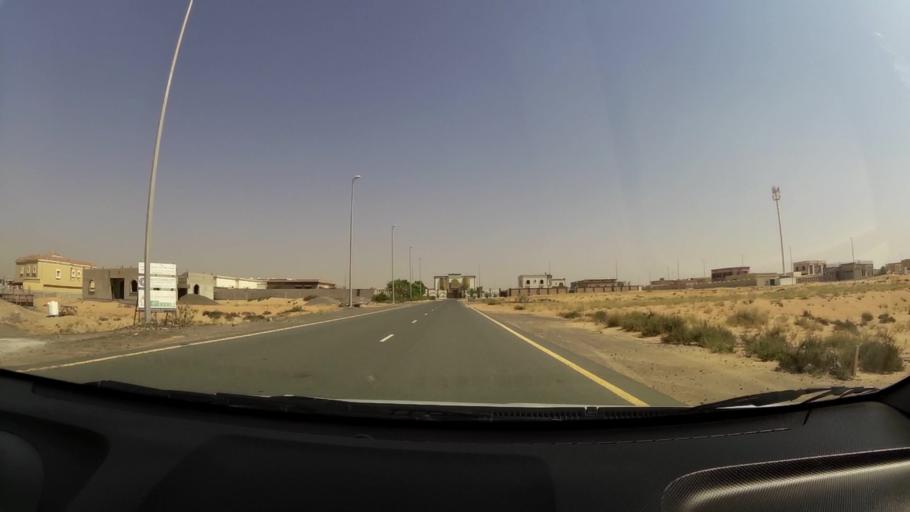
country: AE
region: Umm al Qaywayn
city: Umm al Qaywayn
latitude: 25.4877
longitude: 55.6113
